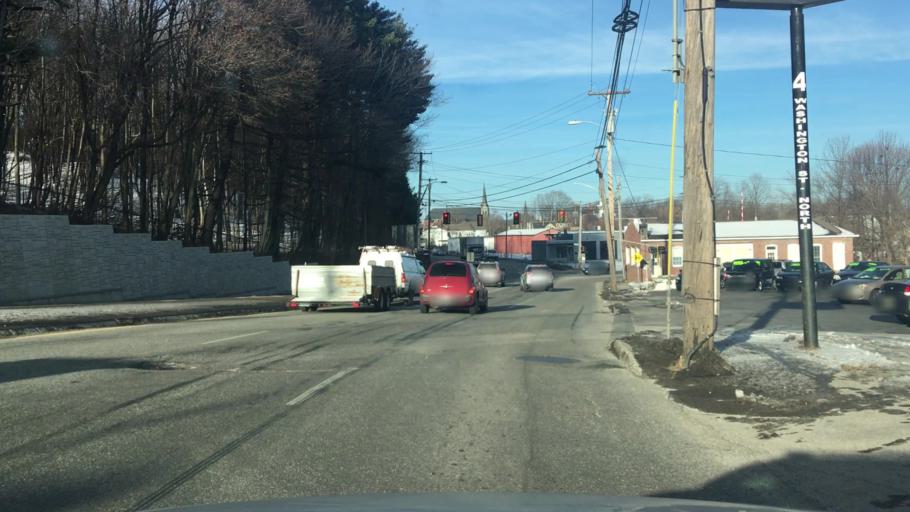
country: US
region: Maine
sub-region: Androscoggin County
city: Auburn
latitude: 44.0901
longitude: -70.2309
